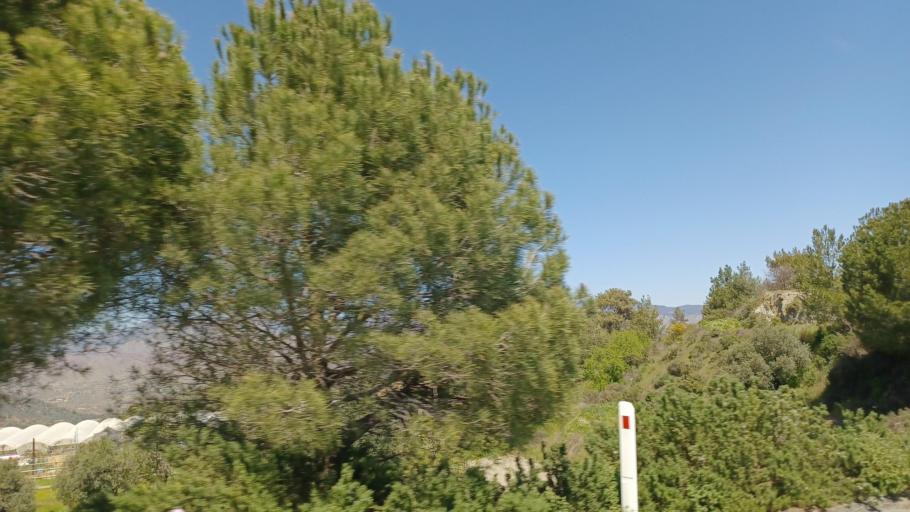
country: CY
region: Limassol
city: Parekklisha
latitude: 34.8084
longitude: 33.1654
